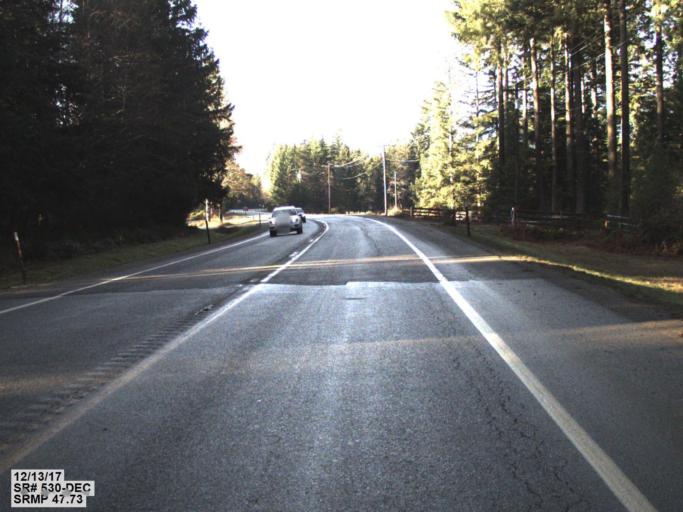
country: US
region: Washington
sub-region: Snohomish County
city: Darrington
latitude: 48.2625
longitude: -121.6280
